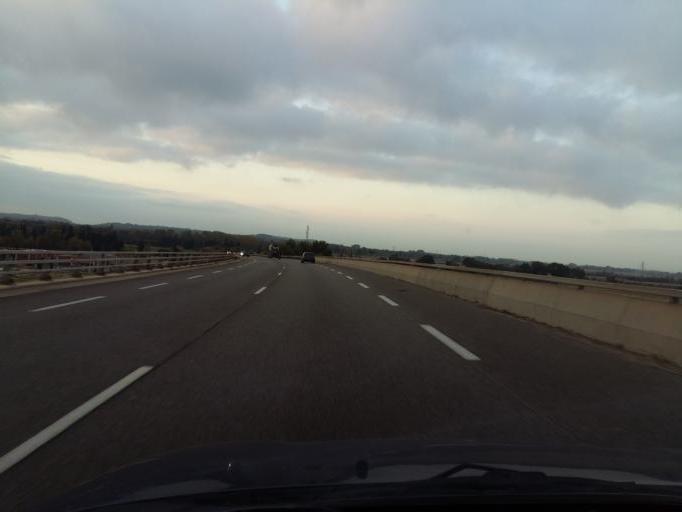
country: FR
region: Provence-Alpes-Cote d'Azur
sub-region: Departement des Bouches-du-Rhone
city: Miramas
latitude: 43.5808
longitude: 4.9844
